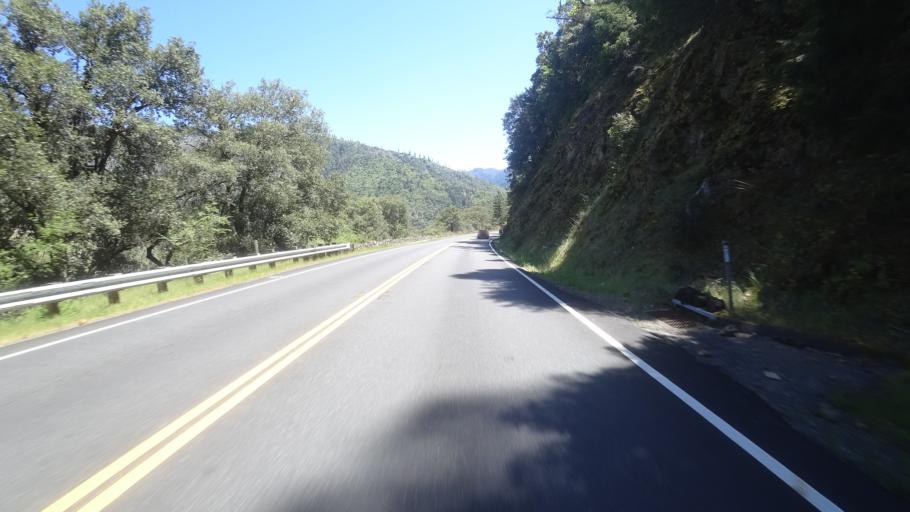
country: US
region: California
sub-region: Humboldt County
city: Willow Creek
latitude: 40.8042
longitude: -123.4671
